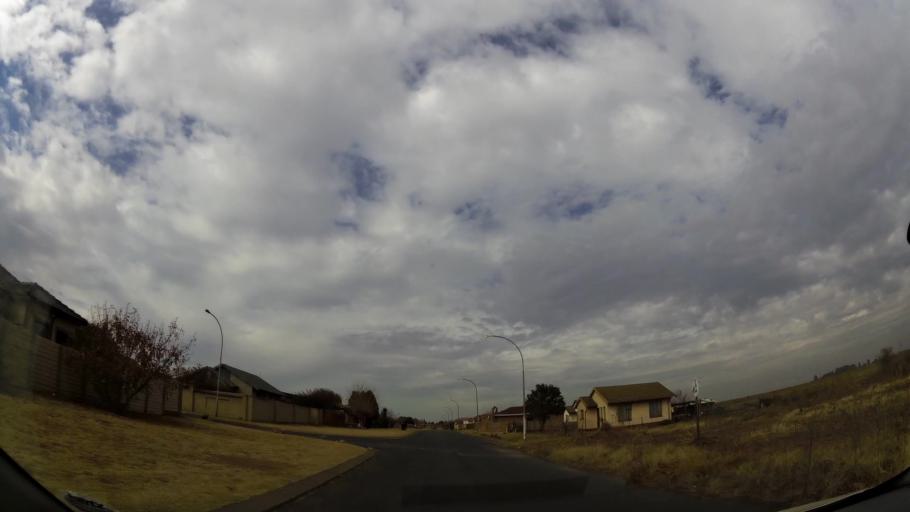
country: ZA
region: Gauteng
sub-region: Ekurhuleni Metropolitan Municipality
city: Germiston
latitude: -26.3145
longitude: 28.1740
